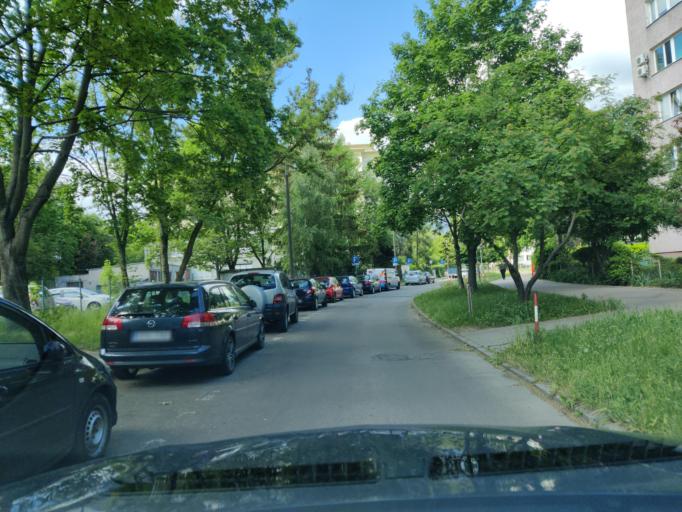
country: PL
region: Masovian Voivodeship
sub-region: Warszawa
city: Mokotow
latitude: 52.1815
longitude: 21.0089
